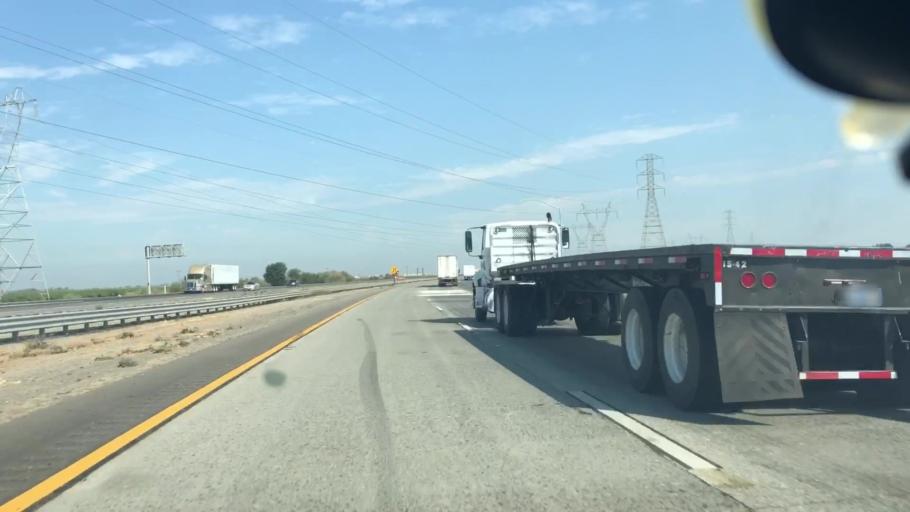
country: US
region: California
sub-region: San Joaquin County
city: Woodbridge
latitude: 38.1204
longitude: -121.3998
